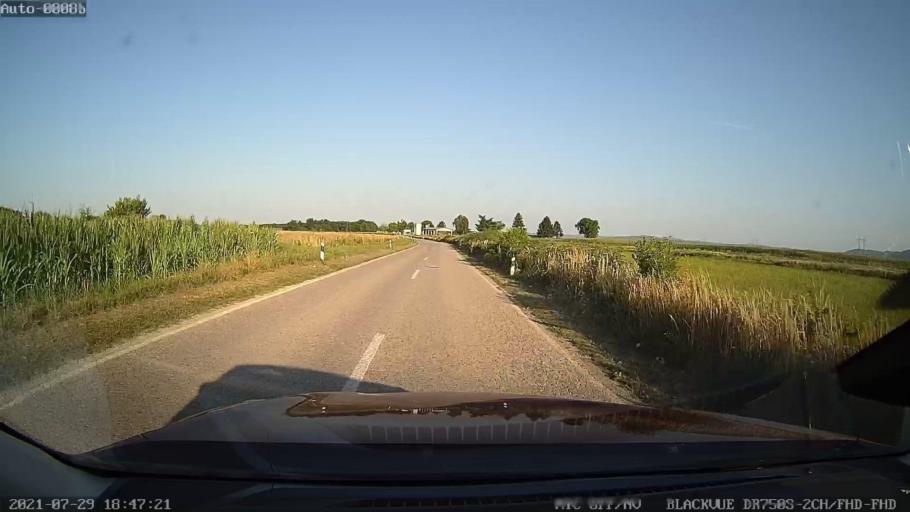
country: HR
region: Varazdinska
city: Sracinec
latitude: 46.3126
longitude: 16.2756
